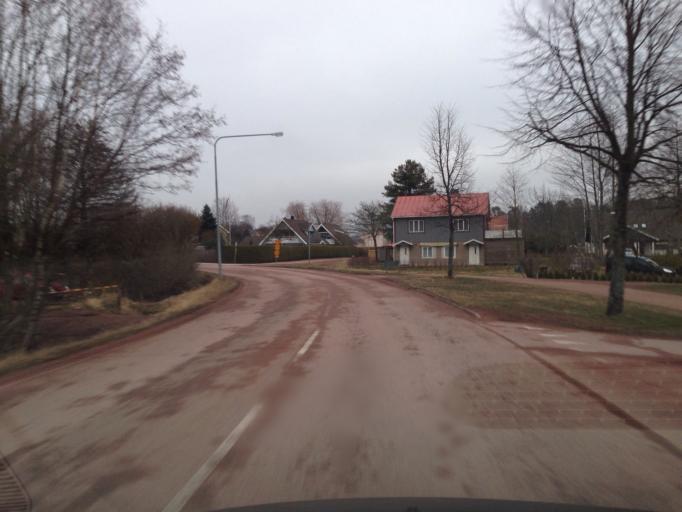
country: AX
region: Mariehamns stad
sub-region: Mariehamn
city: Mariehamn
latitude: 60.1155
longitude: 19.9416
